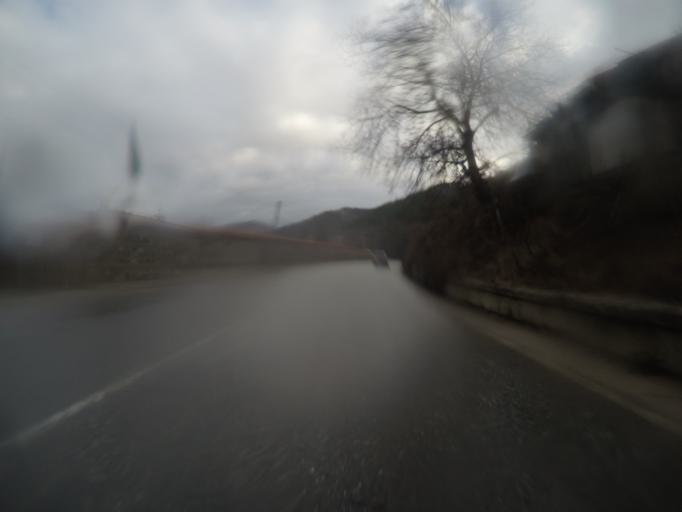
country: BG
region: Blagoevgrad
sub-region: Obshtina Simitli
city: Simitli
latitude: 41.9147
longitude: 23.1921
